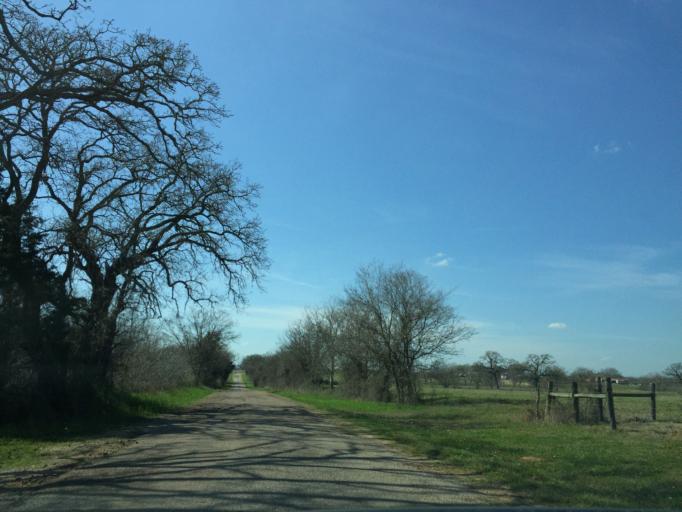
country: US
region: Texas
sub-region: Milam County
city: Thorndale
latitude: 30.5689
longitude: -97.1547
